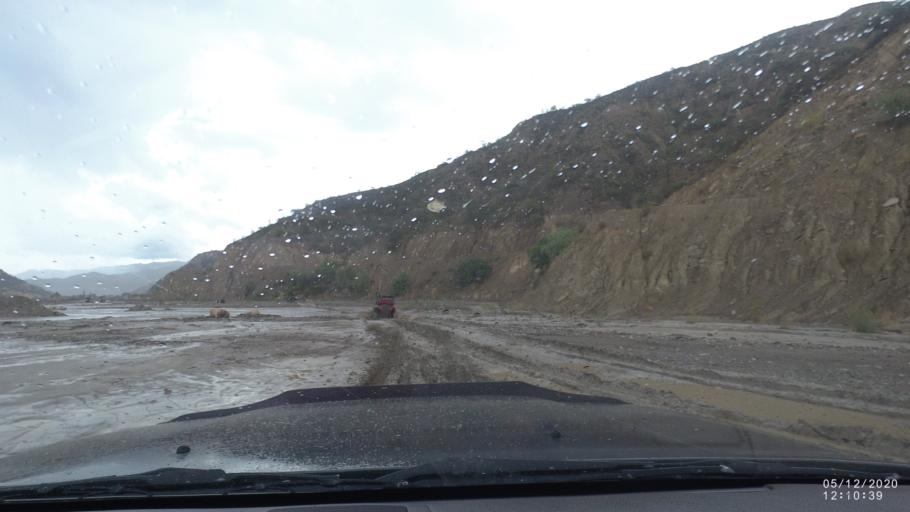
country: BO
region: Cochabamba
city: Sipe Sipe
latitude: -17.5669
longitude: -66.3717
